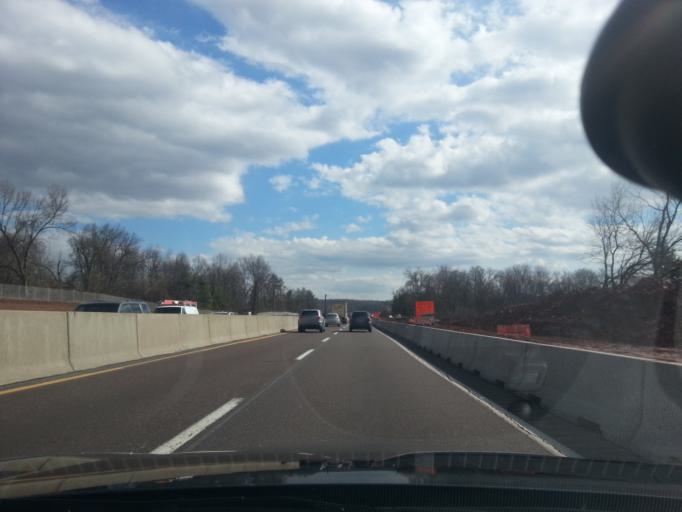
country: US
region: Pennsylvania
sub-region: Montgomery County
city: Kulpsville
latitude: 40.2092
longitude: -75.3234
